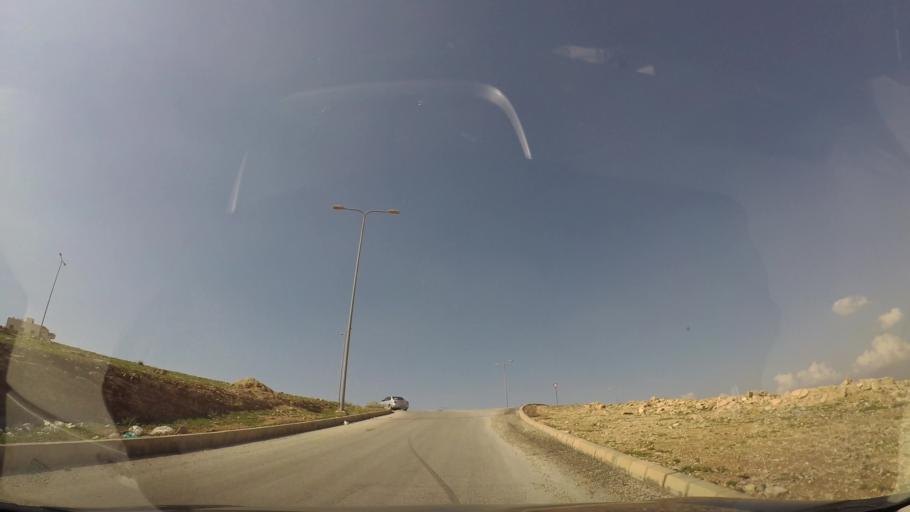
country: JO
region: Zarqa
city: Zarqa
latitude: 32.0495
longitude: 36.1230
